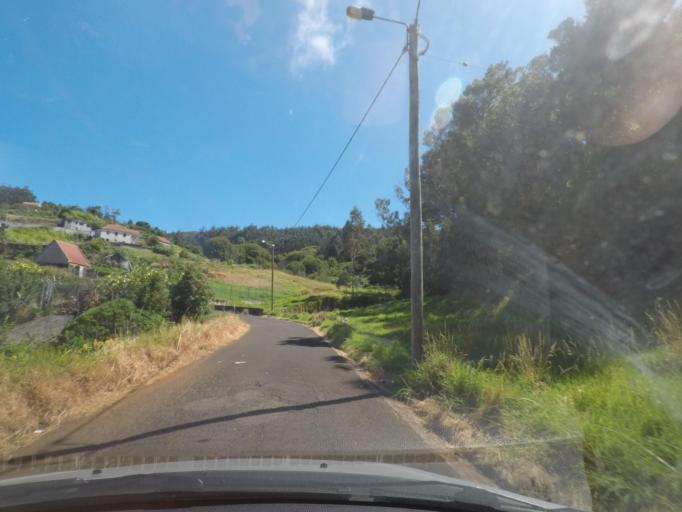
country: PT
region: Madeira
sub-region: Porto Moniz
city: Porto Moniz
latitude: 32.8421
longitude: -17.2076
